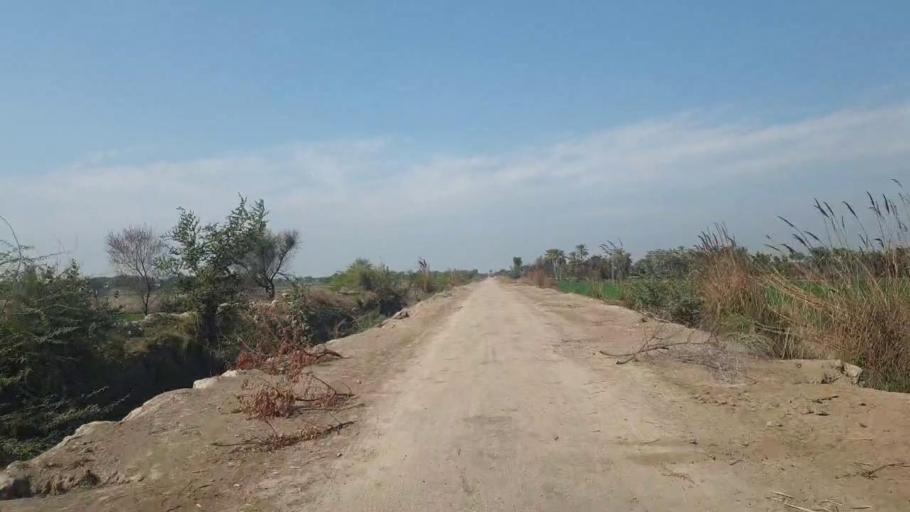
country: PK
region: Sindh
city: Shahdadpur
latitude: 25.9960
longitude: 68.5251
